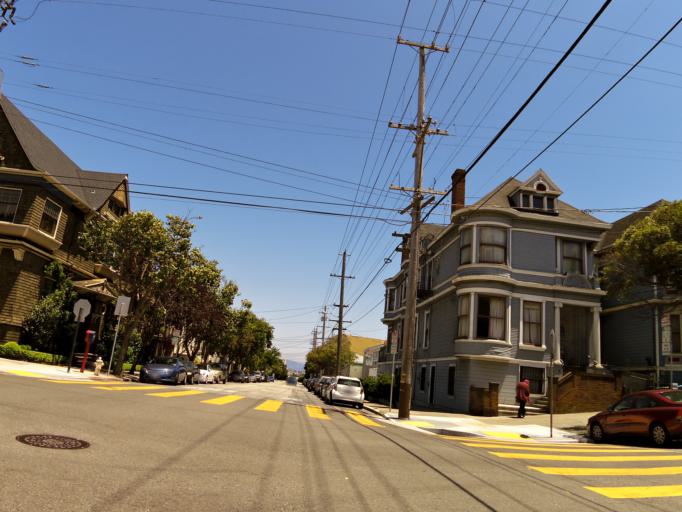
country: US
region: California
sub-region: San Francisco County
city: San Francisco
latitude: 37.7718
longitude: -122.4407
